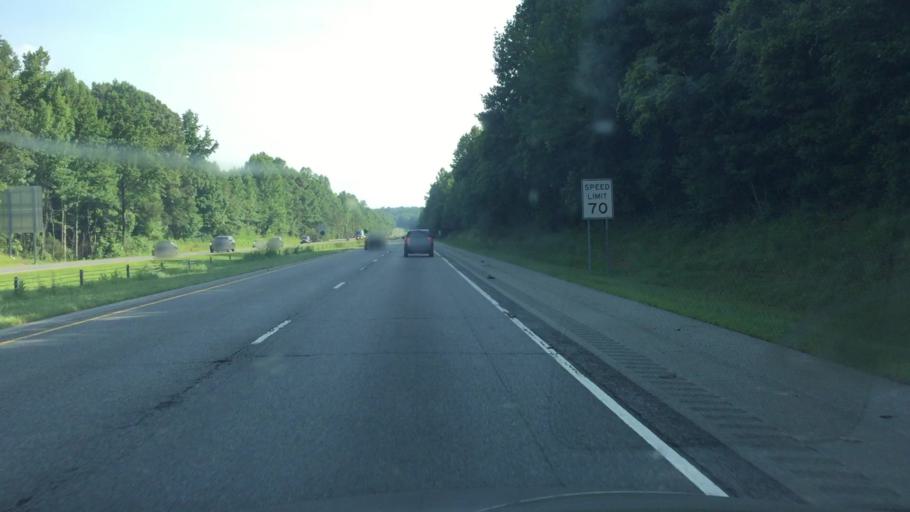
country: US
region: North Carolina
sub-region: Rockingham County
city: Reidsville
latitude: 36.3533
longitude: -79.6317
